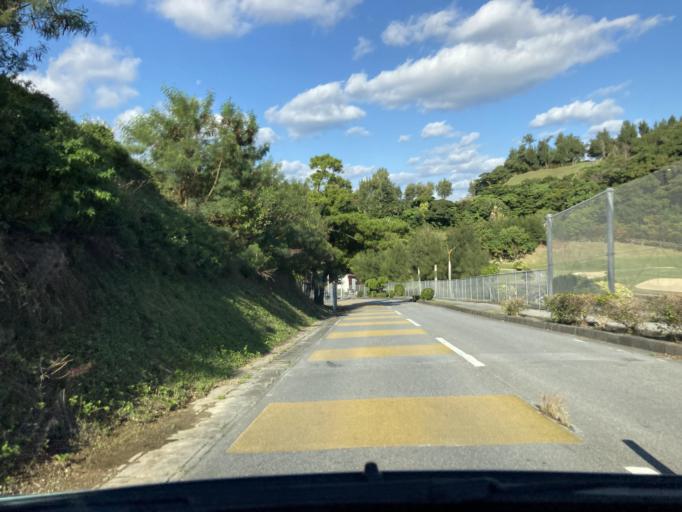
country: JP
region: Okinawa
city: Ginowan
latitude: 26.2156
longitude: 127.7465
